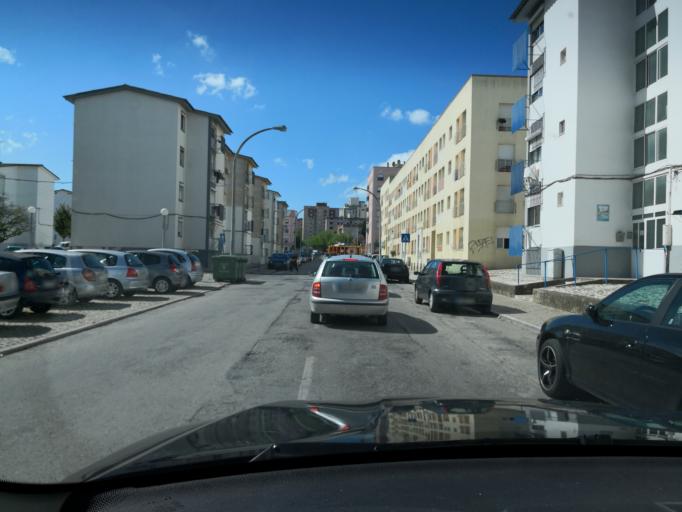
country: PT
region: Setubal
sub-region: Setubal
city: Setubal
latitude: 38.5290
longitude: -8.8704
